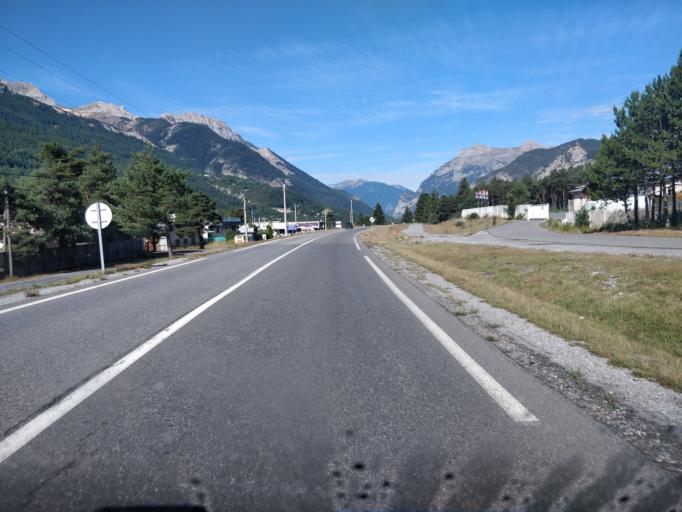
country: FR
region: Provence-Alpes-Cote d'Azur
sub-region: Departement des Alpes-de-Haute-Provence
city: Barcelonnette
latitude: 44.3854
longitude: 6.6077
